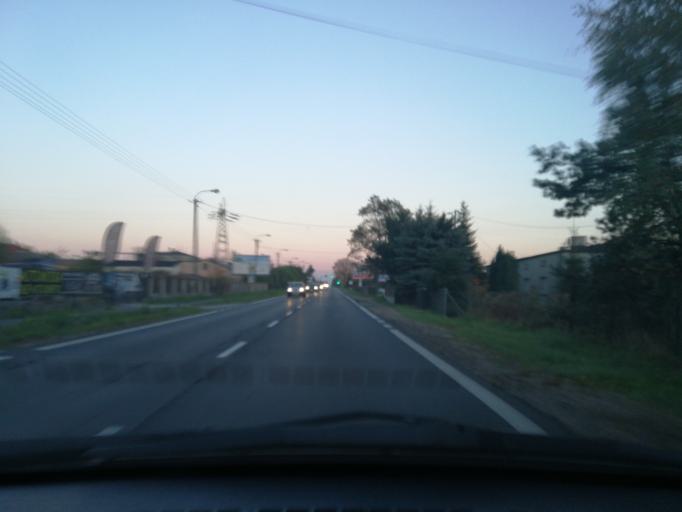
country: PL
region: Lodz Voivodeship
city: Lodz
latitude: 51.7957
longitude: 19.5605
